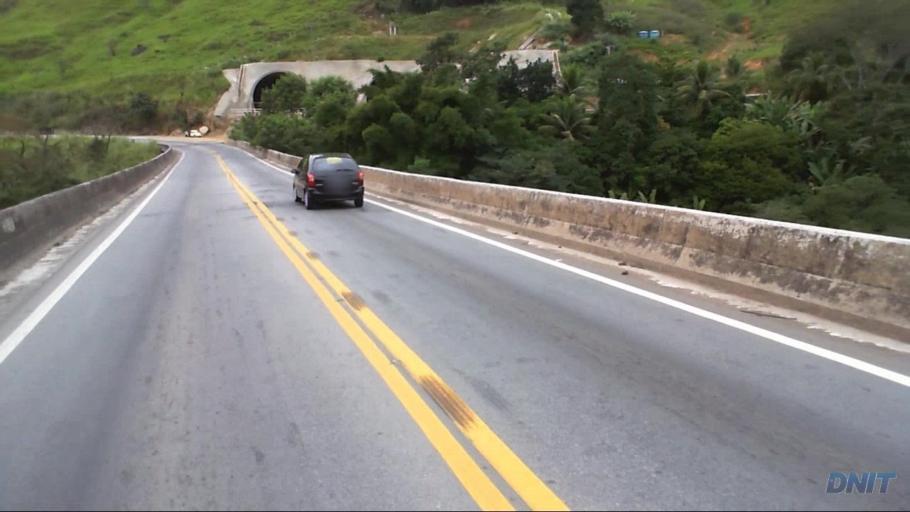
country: BR
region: Minas Gerais
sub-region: Timoteo
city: Timoteo
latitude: -19.6178
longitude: -42.7954
